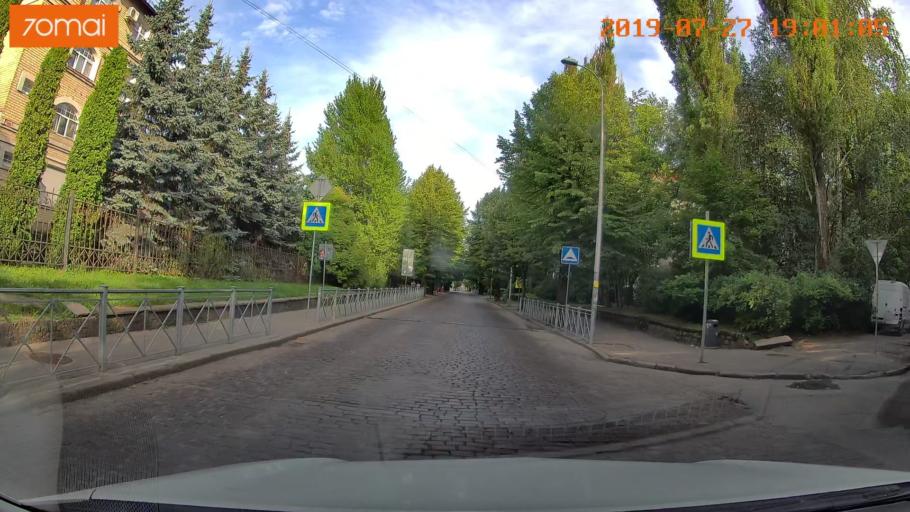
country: RU
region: Kaliningrad
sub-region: Gorod Kaliningrad
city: Kaliningrad
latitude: 54.7271
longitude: 20.4863
